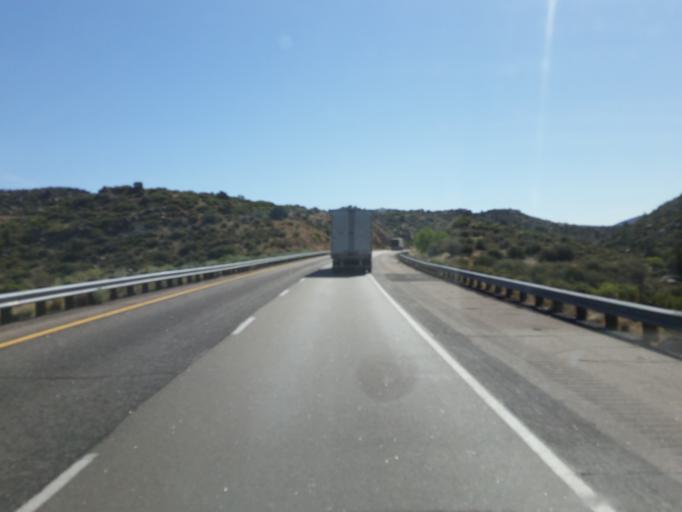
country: US
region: Arizona
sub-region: Mohave County
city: Peach Springs
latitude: 35.1765
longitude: -113.4911
